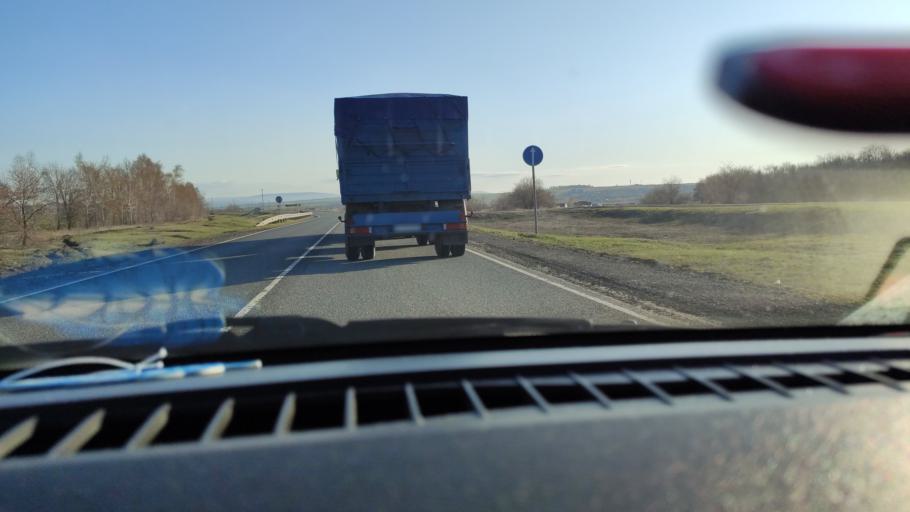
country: RU
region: Saratov
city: Balakovo
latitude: 52.1091
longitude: 47.7468
